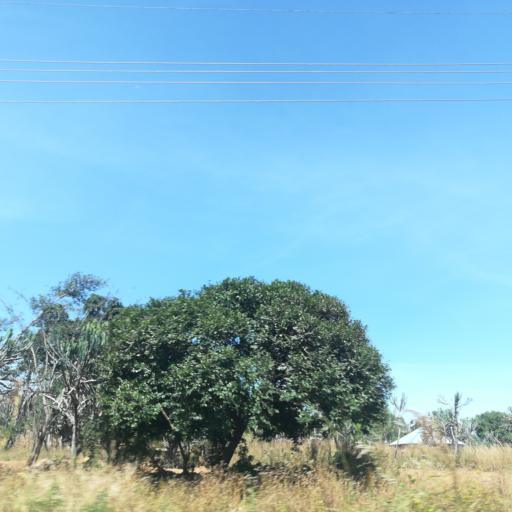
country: NG
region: Plateau
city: Bukuru
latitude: 9.7589
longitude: 8.8792
